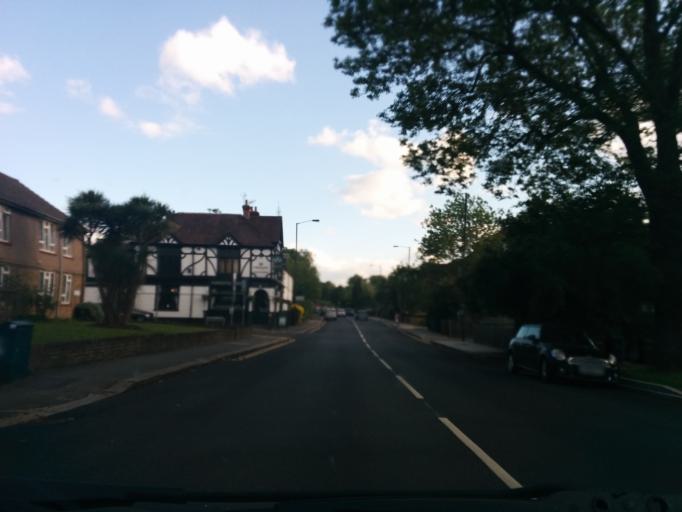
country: GB
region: England
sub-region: Greater London
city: Greenhill
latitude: 51.5757
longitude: -0.3433
